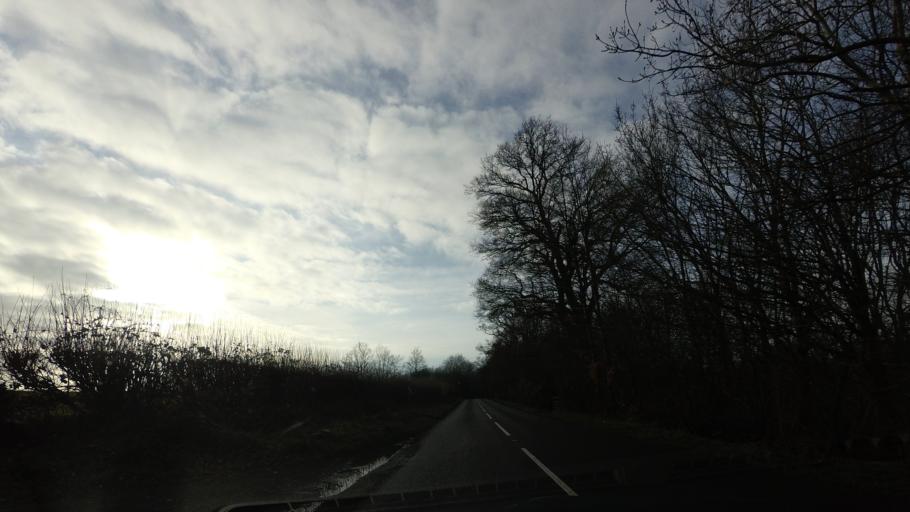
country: GB
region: England
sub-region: East Sussex
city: Battle
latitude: 50.9066
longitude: 0.4817
